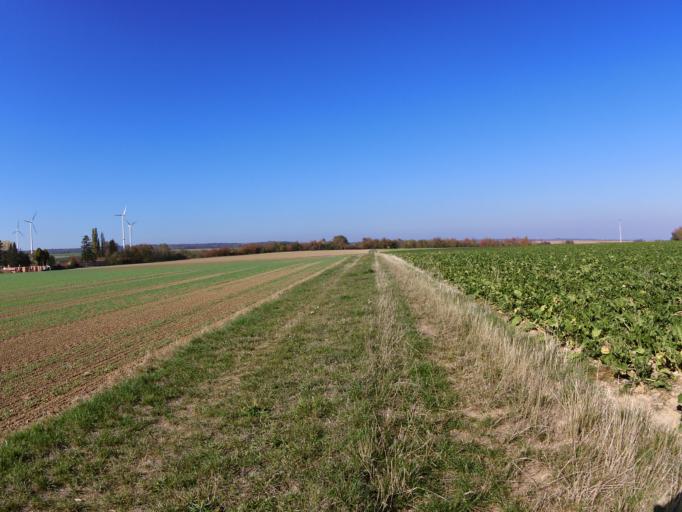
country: DE
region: Bavaria
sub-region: Regierungsbezirk Unterfranken
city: Geroldshausen
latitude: 49.6892
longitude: 9.9088
